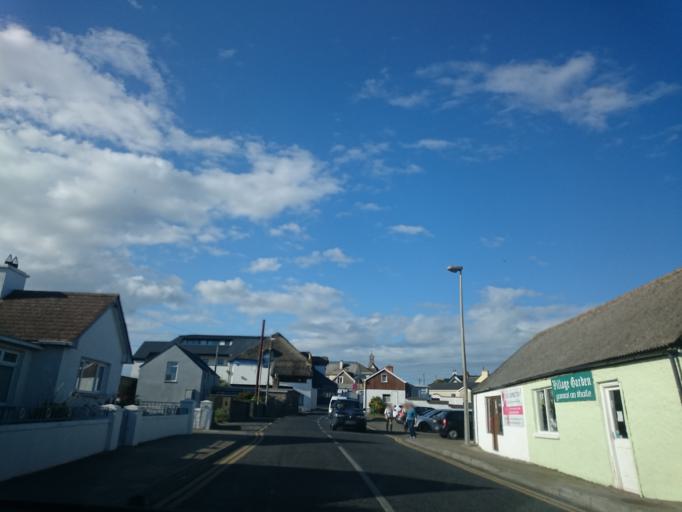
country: IE
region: Leinster
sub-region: Loch Garman
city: Loch Garman
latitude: 52.1731
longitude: -6.5888
